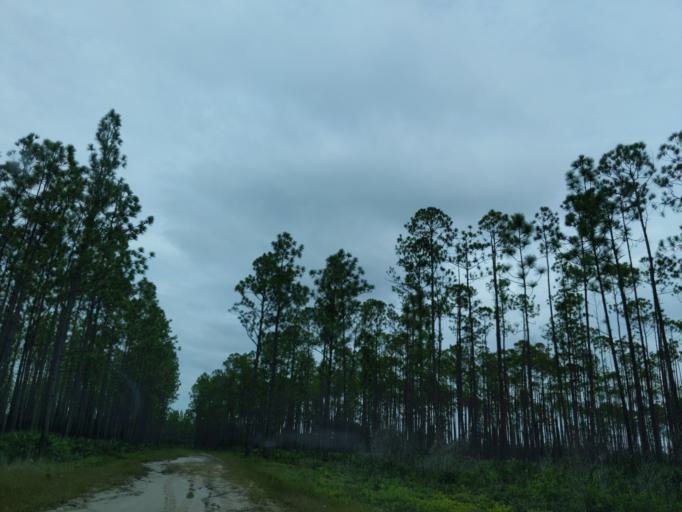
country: US
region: Florida
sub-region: Gadsden County
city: Midway
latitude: 30.3503
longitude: -84.4909
